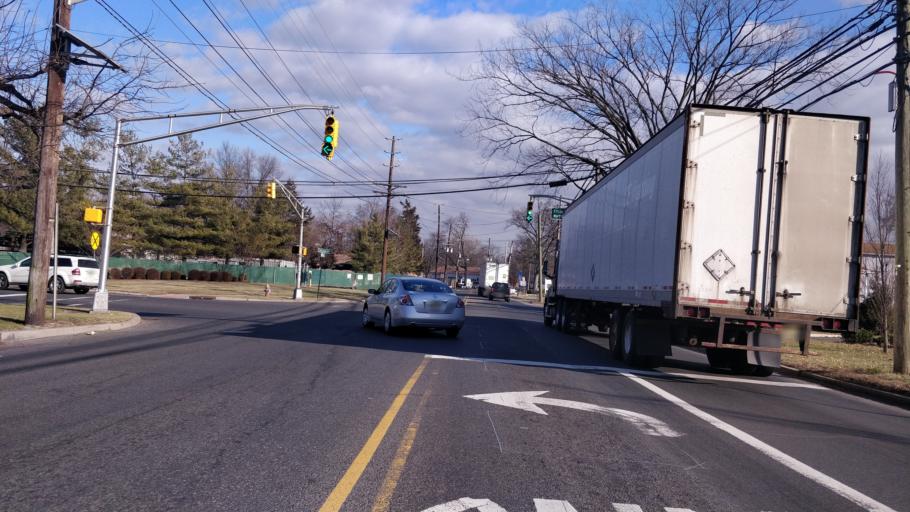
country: US
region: New Jersey
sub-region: Middlesex County
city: South Plainfield
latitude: 40.5803
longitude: -74.4305
